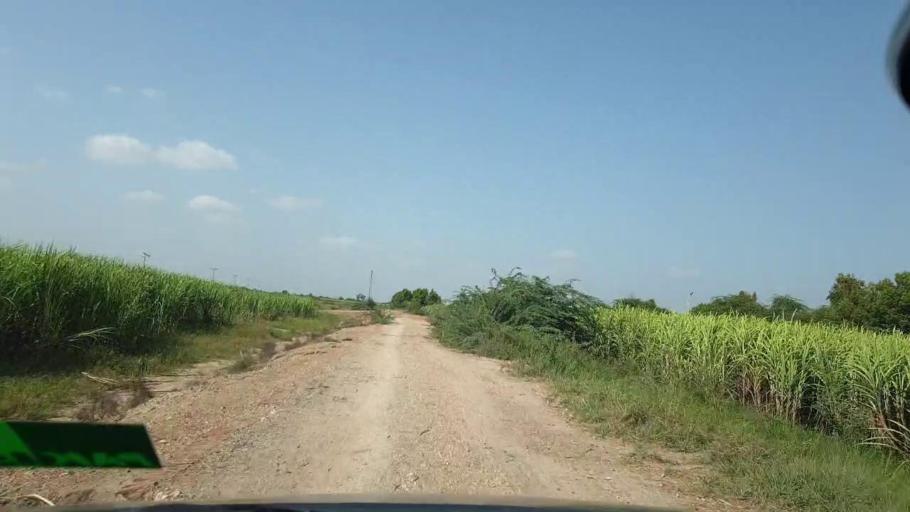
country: PK
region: Sindh
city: Tando Bago
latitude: 24.6837
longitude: 69.2057
